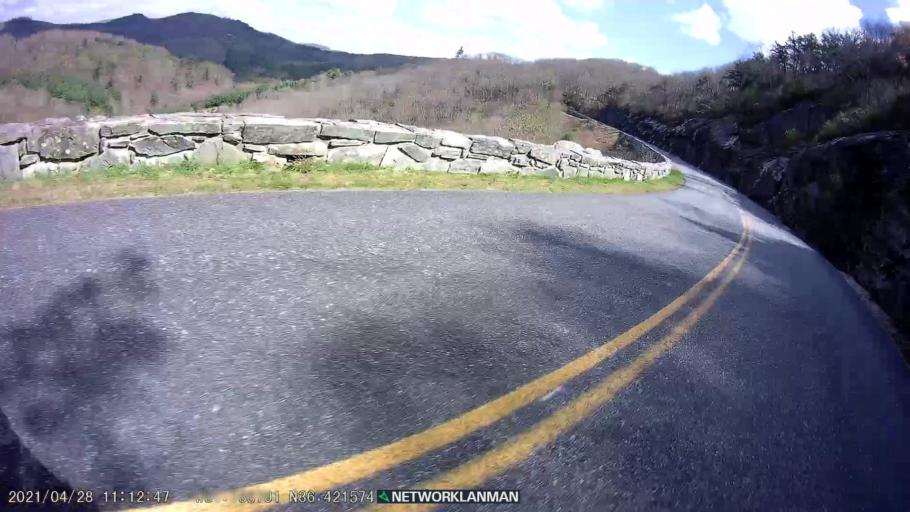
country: US
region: North Carolina
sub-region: Alleghany County
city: Sparta
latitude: 36.4227
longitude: -81.1861
